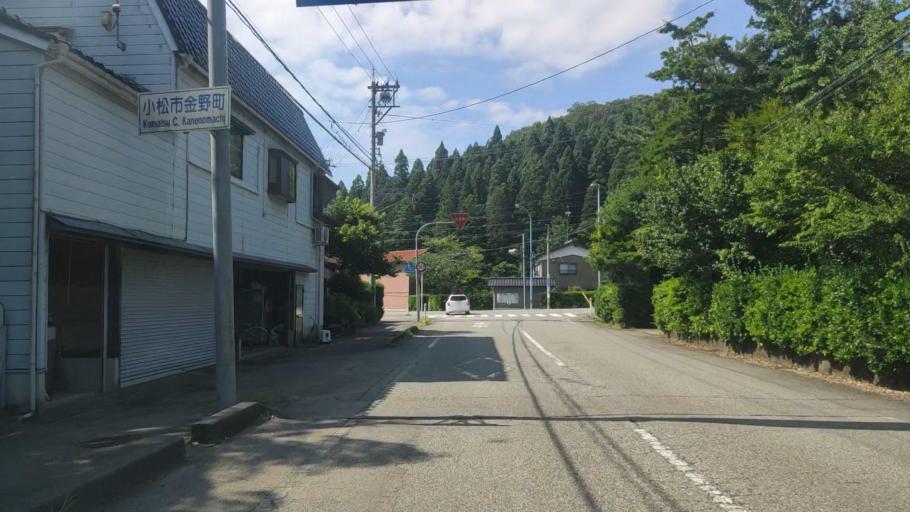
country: JP
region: Ishikawa
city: Komatsu
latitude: 36.3589
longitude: 136.4931
